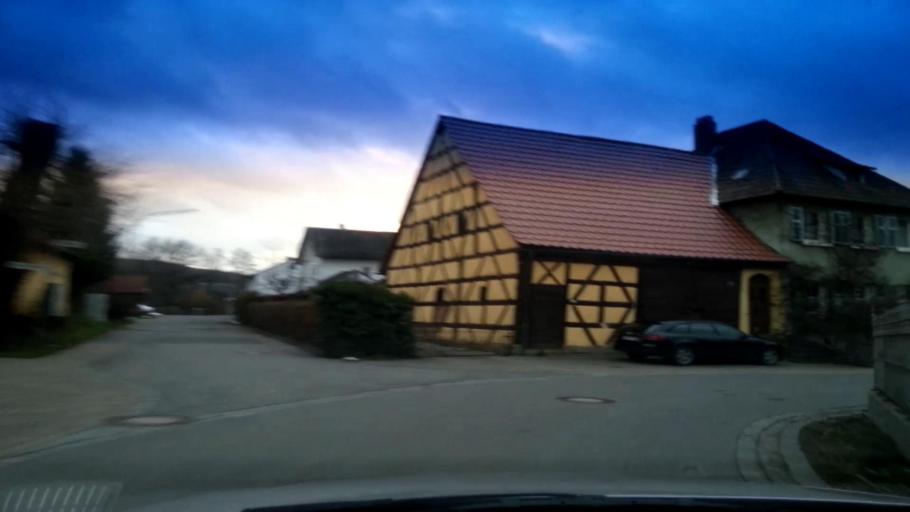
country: DE
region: Bavaria
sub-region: Upper Franconia
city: Schesslitz
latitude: 49.9711
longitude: 11.0582
